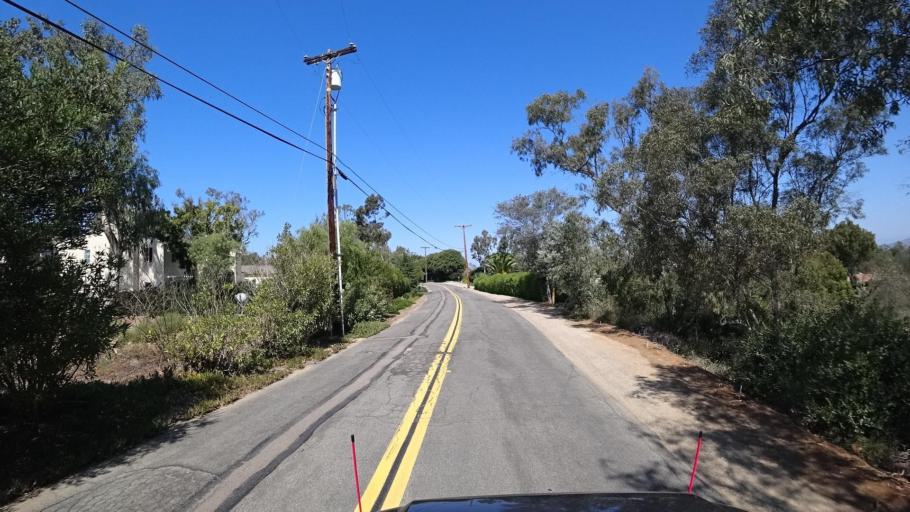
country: US
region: California
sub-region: San Diego County
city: Rancho Santa Fe
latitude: 33.0000
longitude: -117.2213
